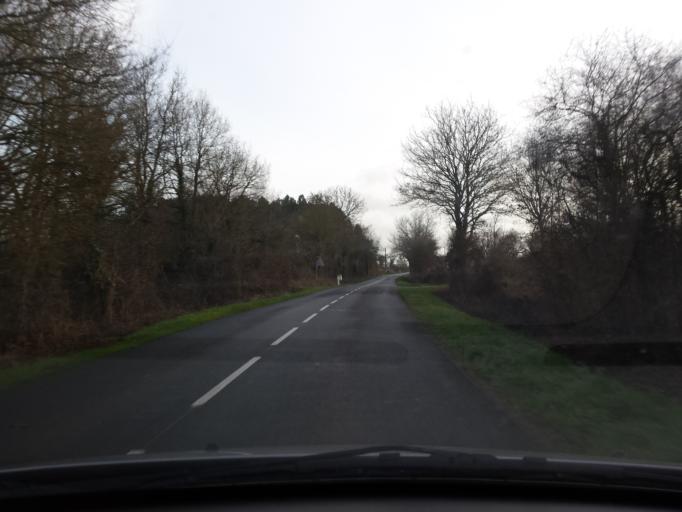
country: FR
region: Pays de la Loire
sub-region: Departement de la Vendee
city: Saint-Florent-des-Bois
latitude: 46.6157
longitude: -1.3081
